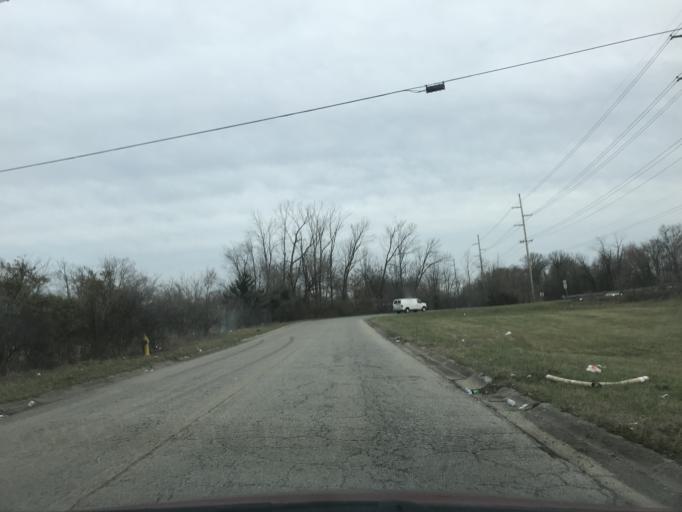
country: US
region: Kentucky
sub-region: Jefferson County
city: West Buechel
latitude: 38.1891
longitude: -85.6698
